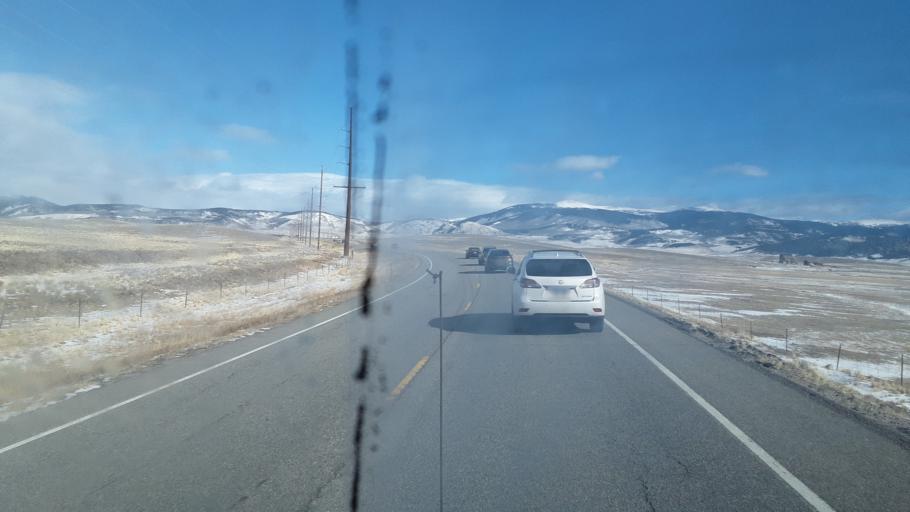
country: US
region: Colorado
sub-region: Park County
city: Fairplay
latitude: 39.3565
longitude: -105.8201
